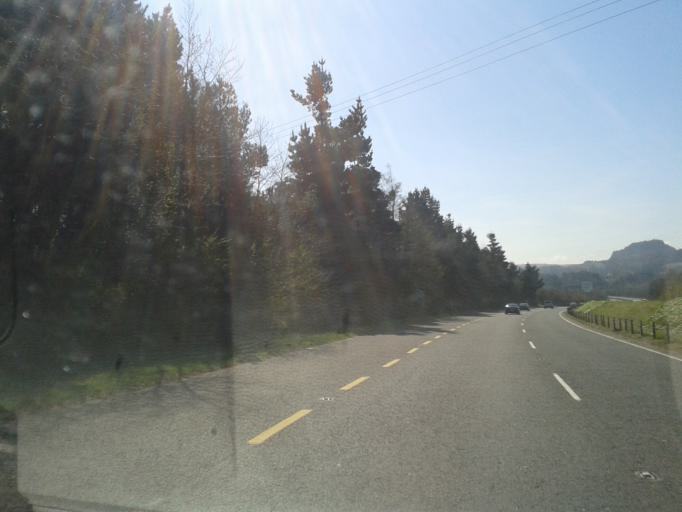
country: IE
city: Kilquade
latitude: 53.0809
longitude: -6.0893
